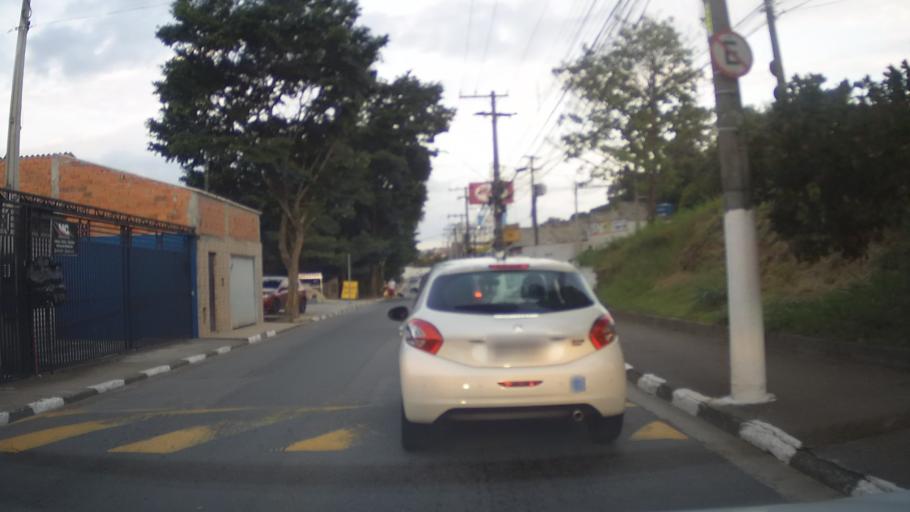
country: BR
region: Sao Paulo
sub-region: Aruja
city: Aruja
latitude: -23.3968
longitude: -46.3304
